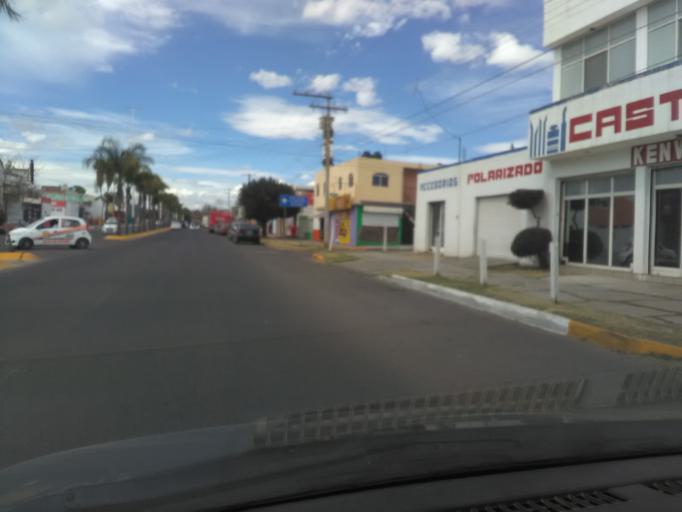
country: MX
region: Durango
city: Victoria de Durango
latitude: 24.0390
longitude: -104.6669
